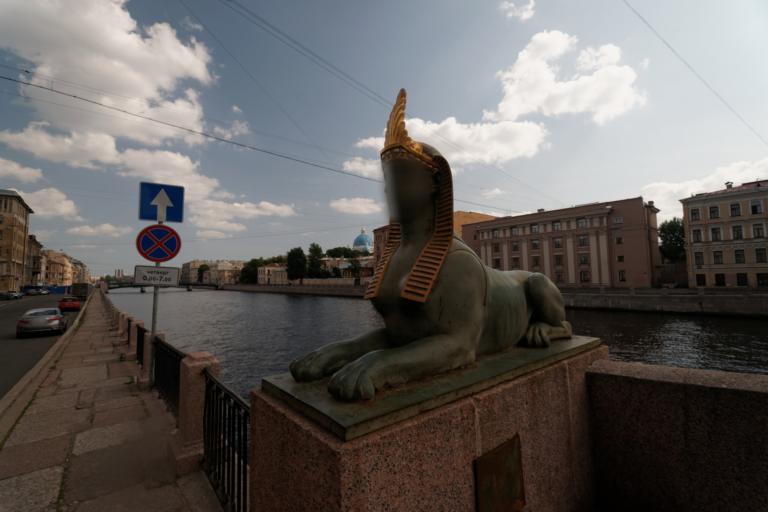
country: RU
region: St.-Petersburg
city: Admiralteisky
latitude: 59.9173
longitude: 30.2976
